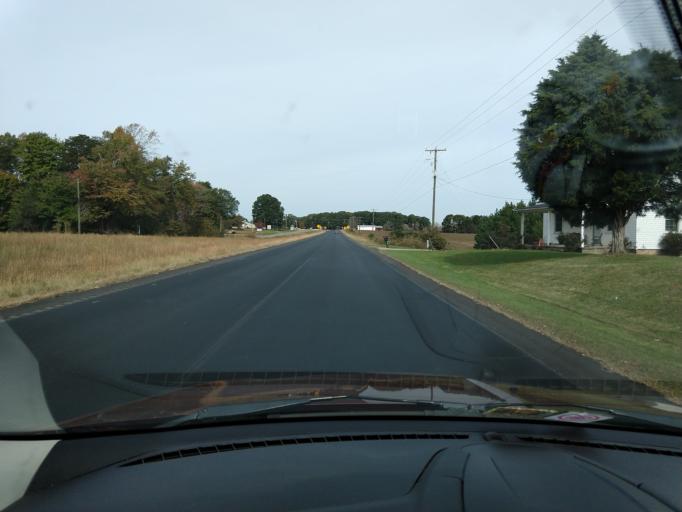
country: US
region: Virginia
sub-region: Pittsylvania County
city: Chatham
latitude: 36.8605
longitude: -79.3999
